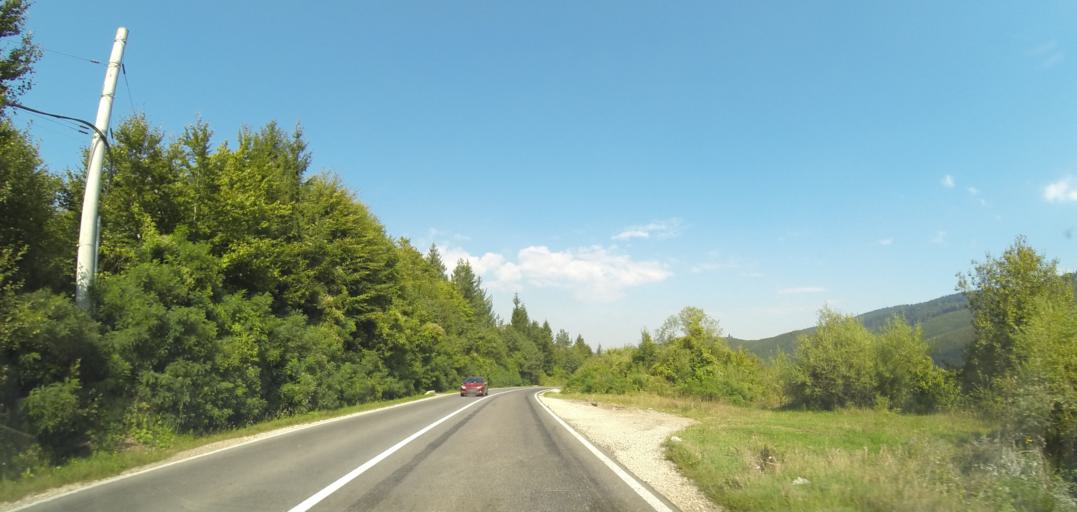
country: RO
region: Brasov
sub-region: Comuna Tarlungeni
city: Tarlungeni
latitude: 45.5822
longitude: 25.7585
